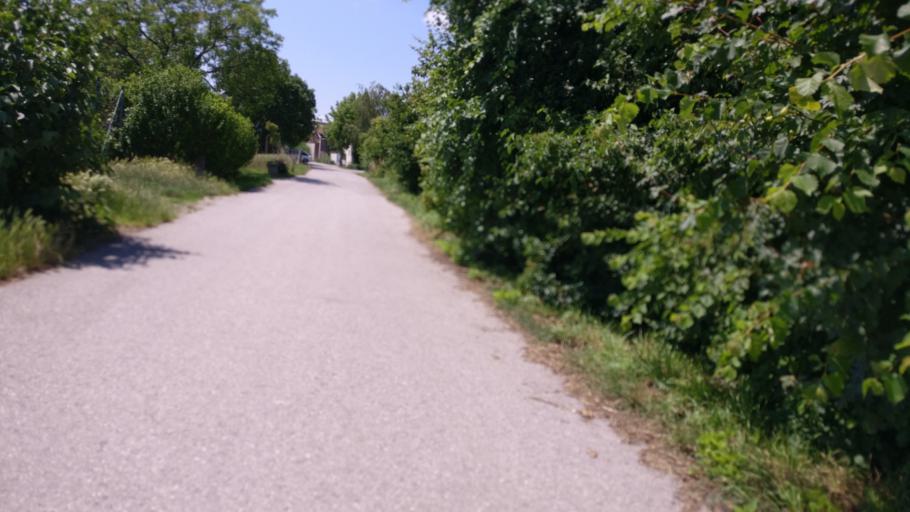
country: AT
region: Lower Austria
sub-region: Politischer Bezirk Baden
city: Schonau an der Triesting
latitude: 47.9353
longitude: 16.2567
